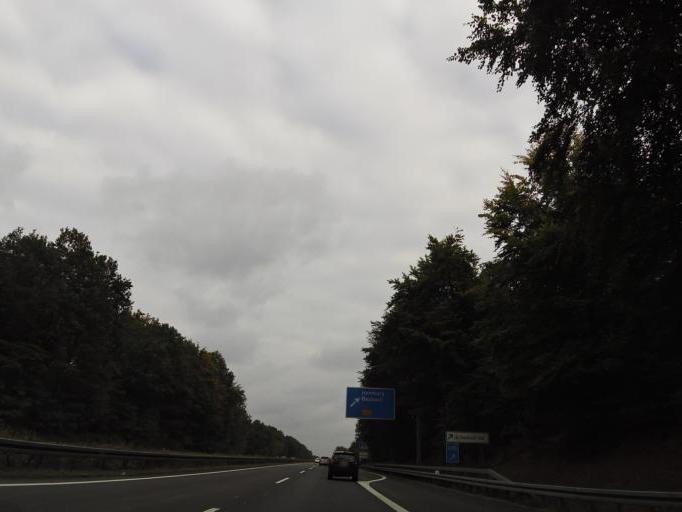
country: DE
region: Saarland
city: Bexbach
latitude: 49.3380
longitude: 7.2932
